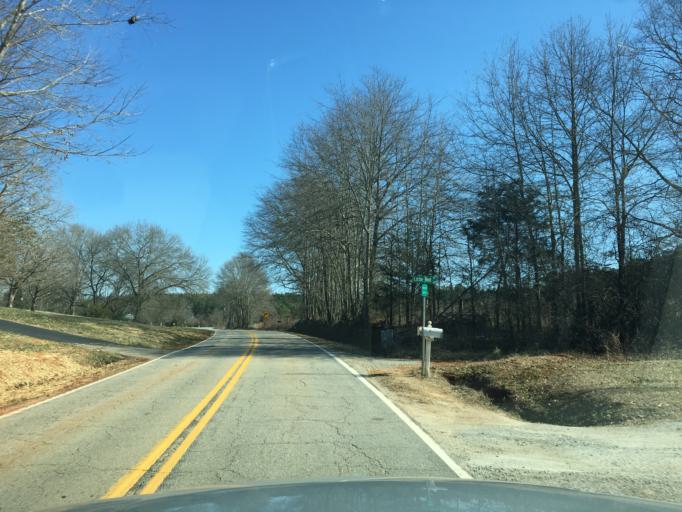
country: US
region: South Carolina
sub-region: Pickens County
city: Liberty
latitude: 34.7932
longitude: -82.7209
